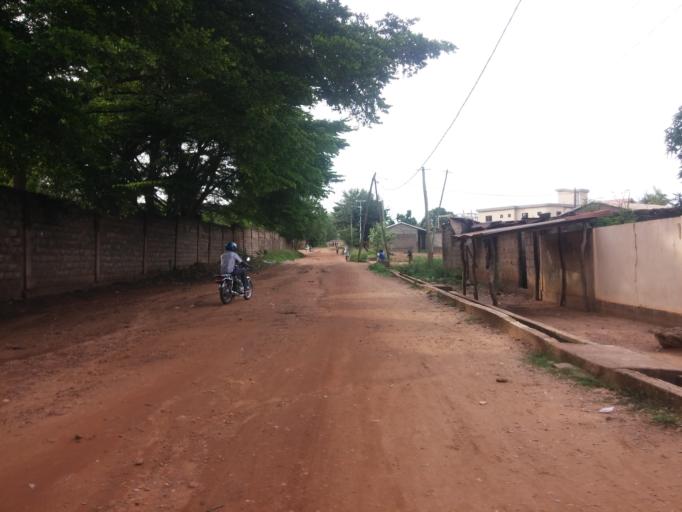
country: TG
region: Kara
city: Kara
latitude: 9.5461
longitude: 1.2029
